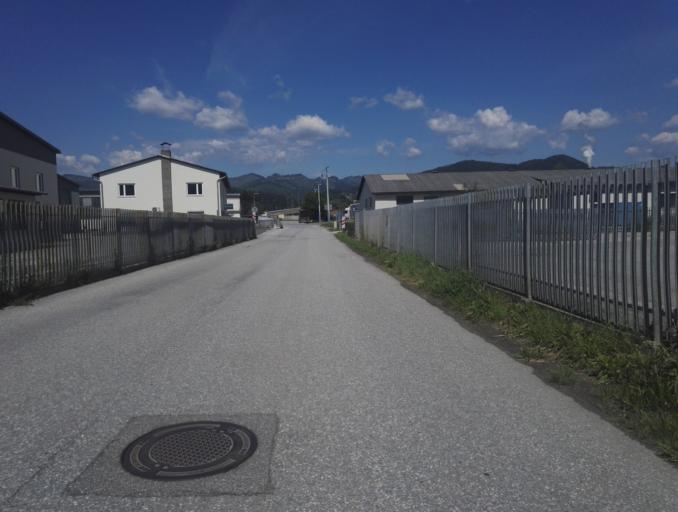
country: AT
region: Styria
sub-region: Politischer Bezirk Graz-Umgebung
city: Gratkorn
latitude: 47.1252
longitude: 15.3352
